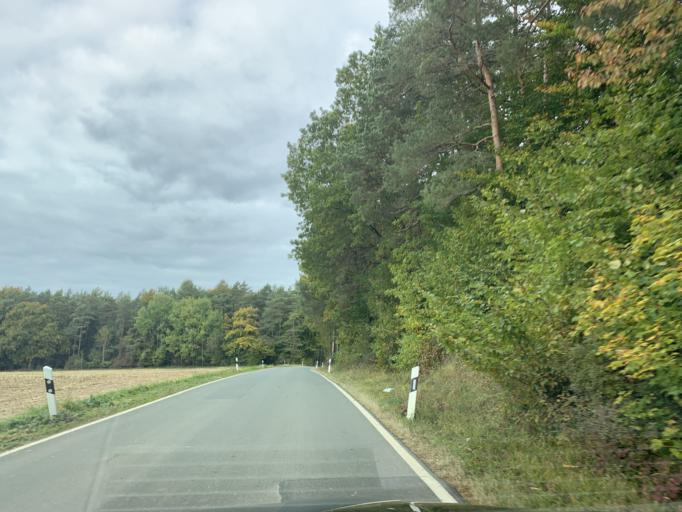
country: DE
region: Bavaria
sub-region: Upper Franconia
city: Unterleinleiter
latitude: 49.8342
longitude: 11.2548
